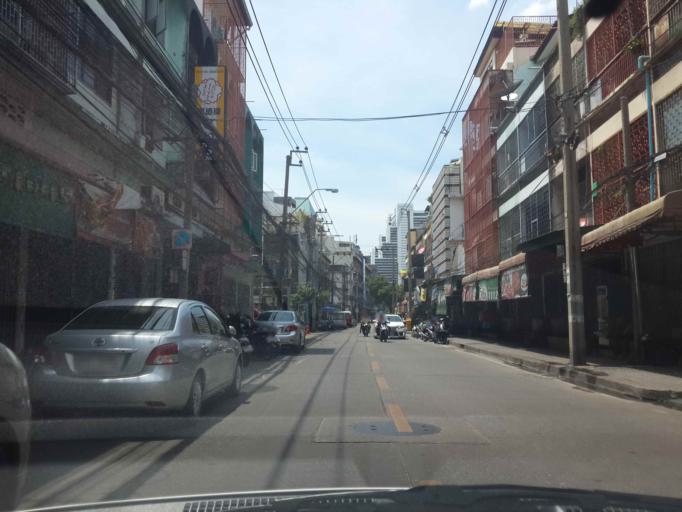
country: TH
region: Bangkok
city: Khlong Toei
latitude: 13.7239
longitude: 100.5649
